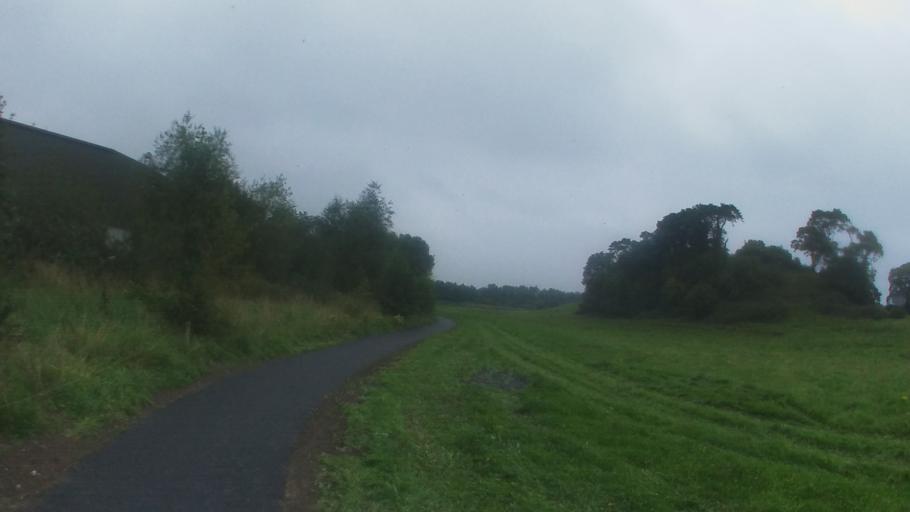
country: IE
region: Leinster
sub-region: Kilkenny
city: Callan
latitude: 52.5456
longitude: -7.3920
